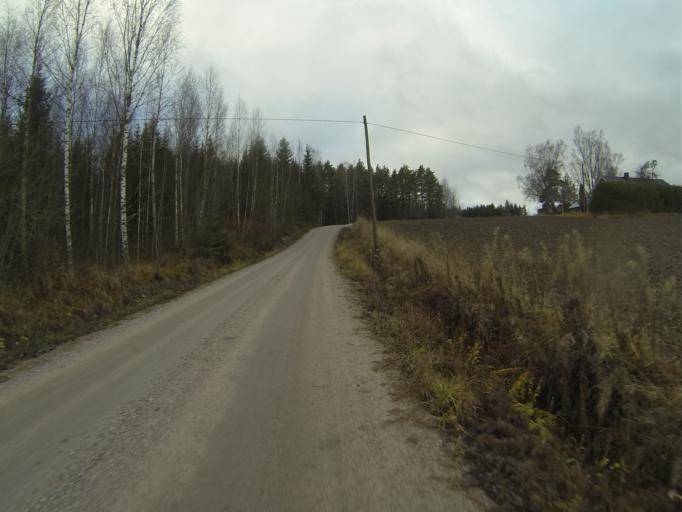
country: FI
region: Varsinais-Suomi
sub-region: Salo
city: Halikko
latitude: 60.4033
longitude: 22.9980
